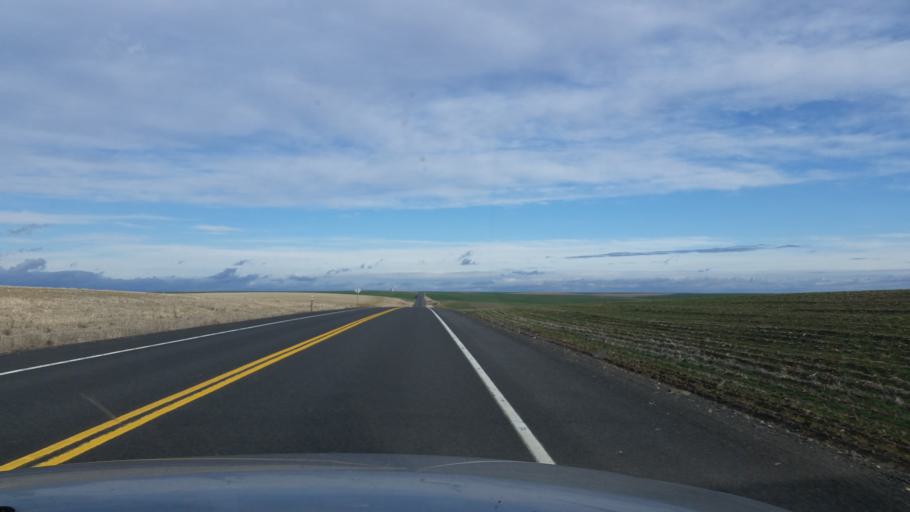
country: US
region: Washington
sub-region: Adams County
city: Ritzville
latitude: 47.3966
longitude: -118.4004
